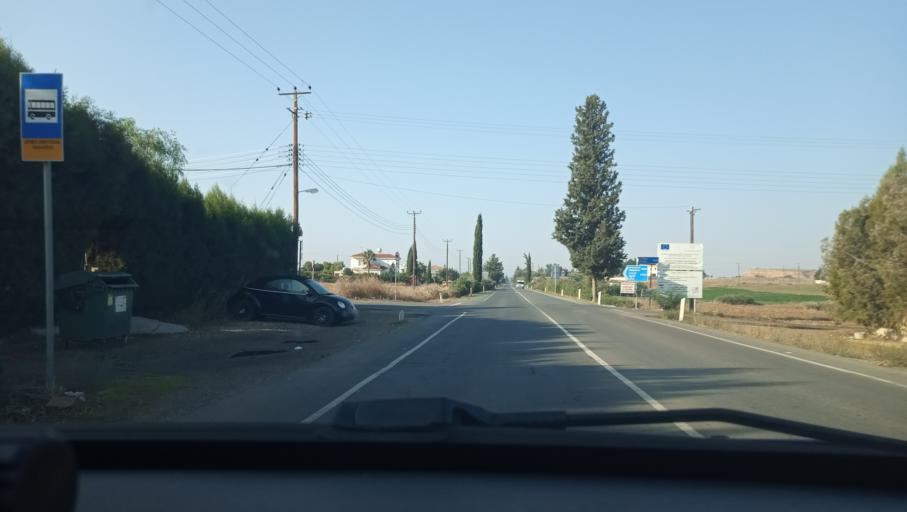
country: CY
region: Lefkosia
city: Kato Deftera
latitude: 35.0896
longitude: 33.2667
